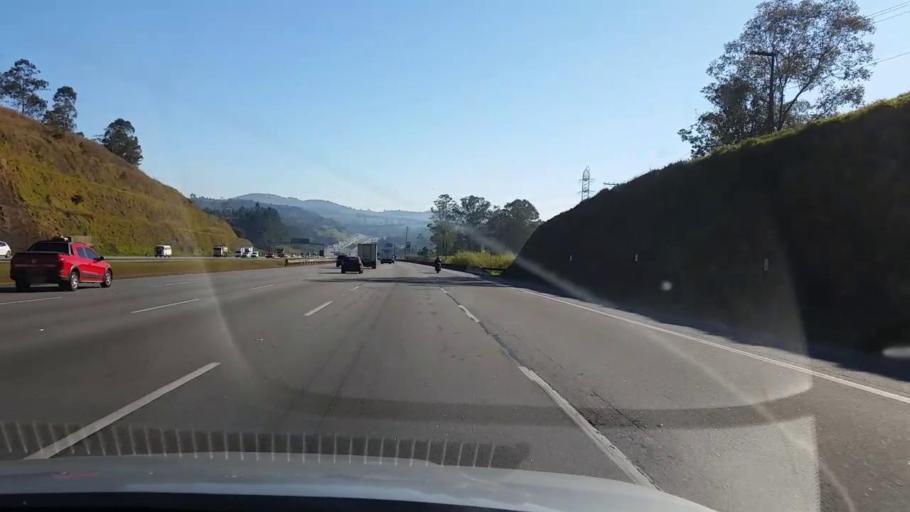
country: BR
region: Sao Paulo
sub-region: Caieiras
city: Caieiras
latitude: -23.4017
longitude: -46.7676
